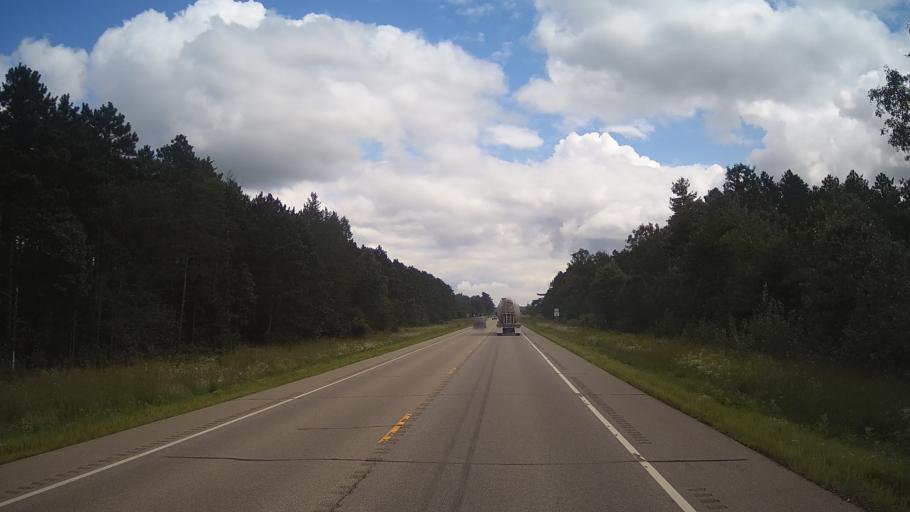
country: US
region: Wisconsin
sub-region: Marquette County
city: Westfield
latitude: 44.0220
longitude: -89.6233
